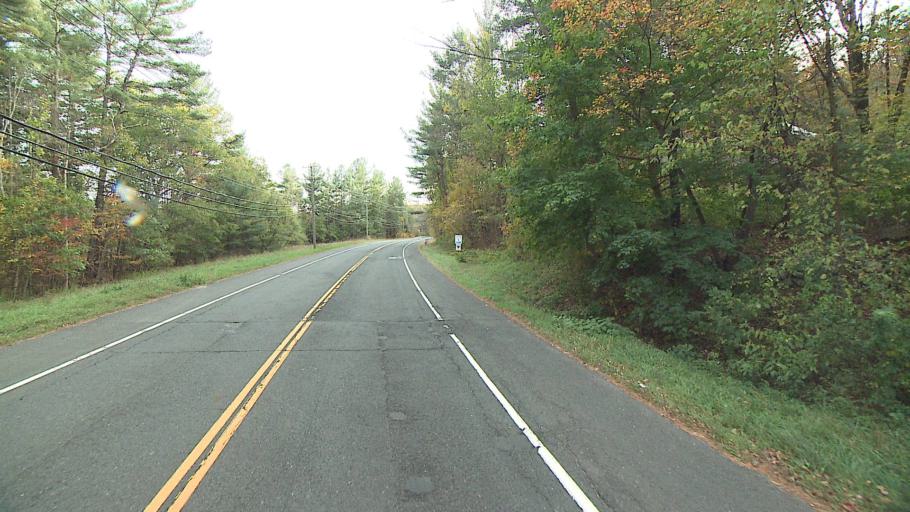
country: US
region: Connecticut
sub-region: Litchfield County
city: New Hartford Center
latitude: 41.8919
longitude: -72.9852
